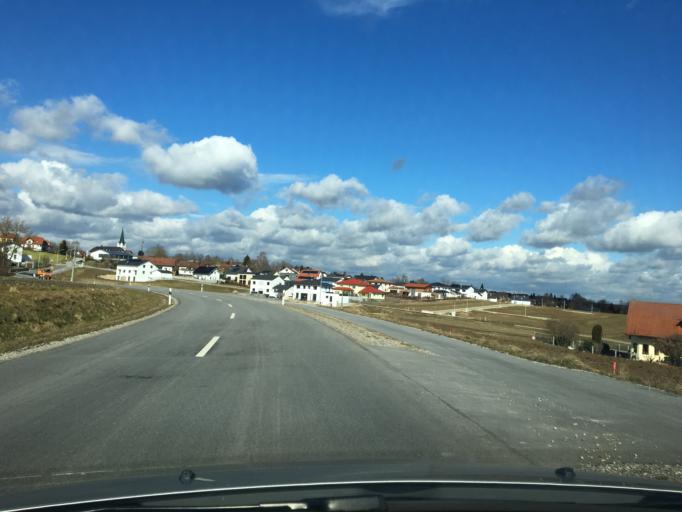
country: DE
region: Bavaria
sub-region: Lower Bavaria
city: Tiefenbach
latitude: 48.4803
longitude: 12.0974
